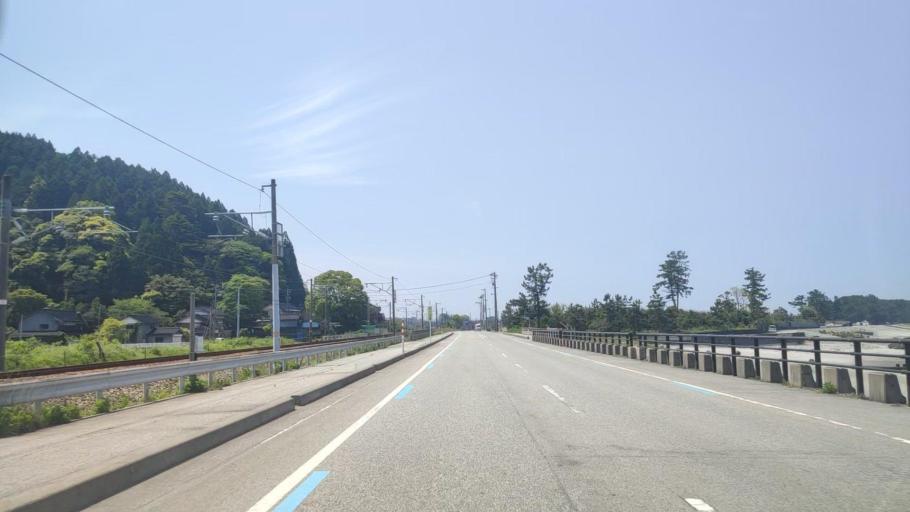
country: JP
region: Toyama
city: Nyuzen
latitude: 36.9644
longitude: 137.5755
